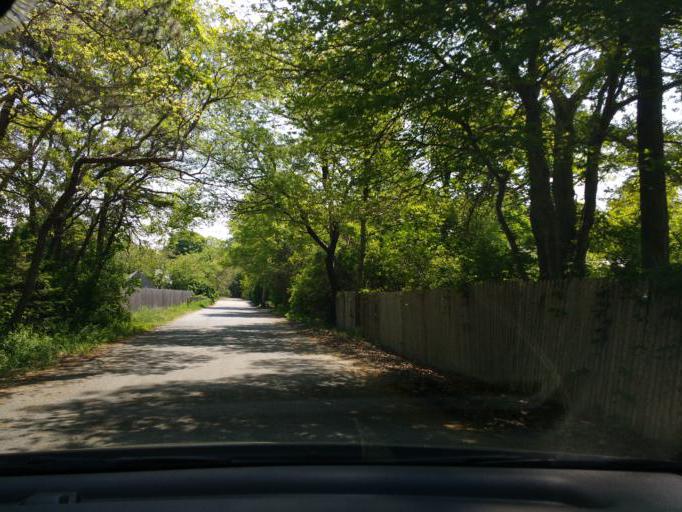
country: US
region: Massachusetts
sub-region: Barnstable County
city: East Falmouth
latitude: 41.5909
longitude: -70.5815
